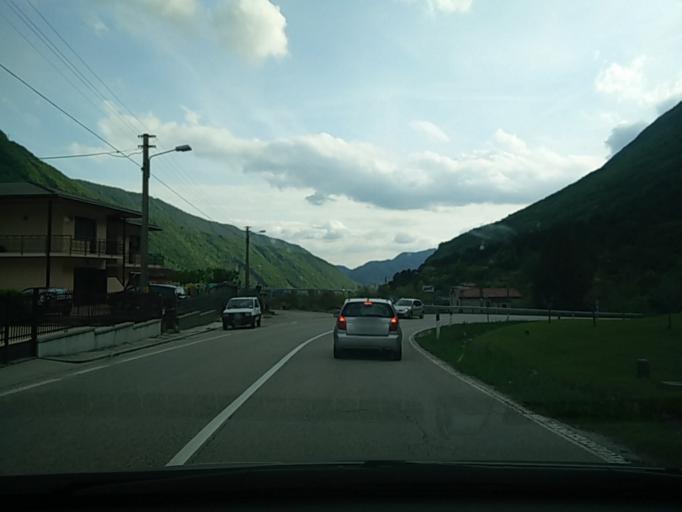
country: IT
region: Veneto
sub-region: Provincia di Treviso
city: Fregona
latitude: 46.0456
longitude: 12.3085
